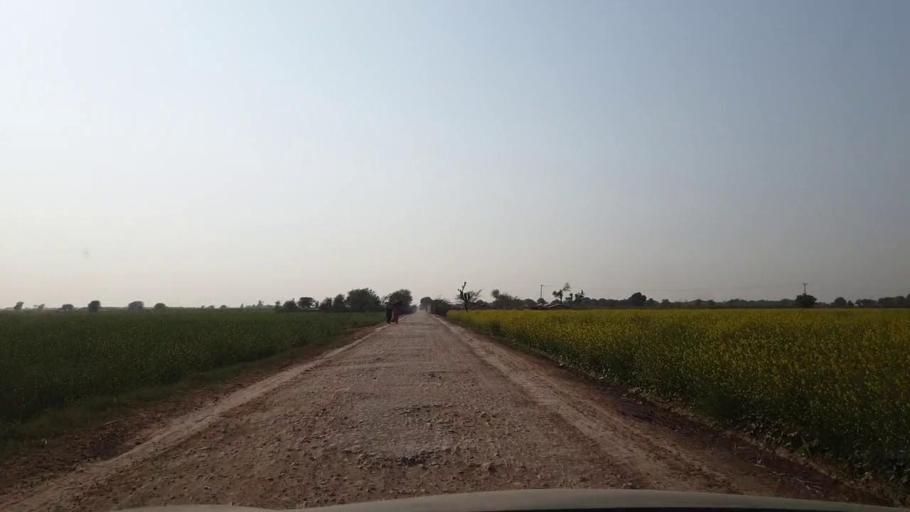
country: PK
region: Sindh
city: Tando Allahyar
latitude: 25.5817
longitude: 68.7928
